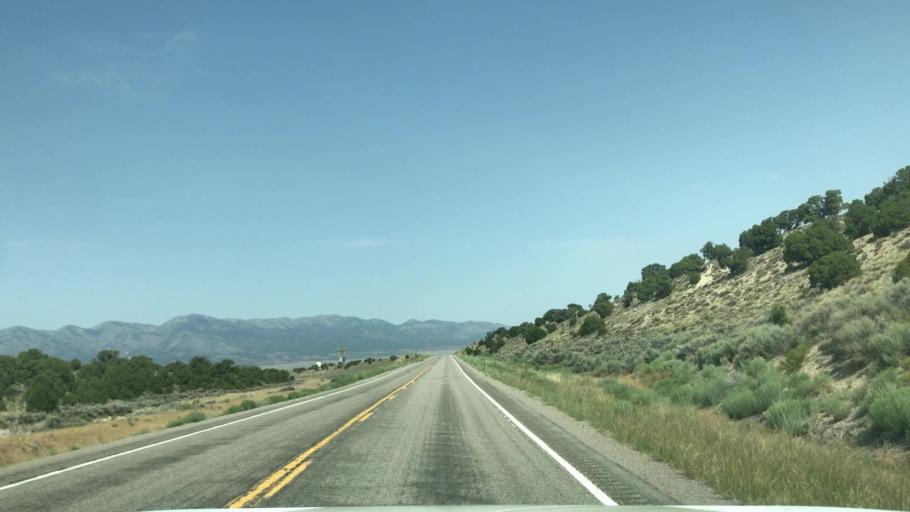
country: US
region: Nevada
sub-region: White Pine County
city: Ely
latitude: 39.0349
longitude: -114.7061
